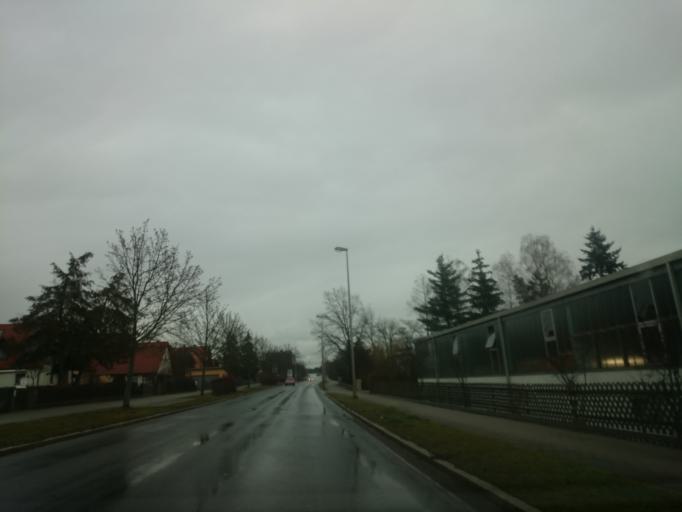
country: DE
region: Bavaria
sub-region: Regierungsbezirk Mittelfranken
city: Hilpoltstein
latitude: 49.1953
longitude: 11.1973
